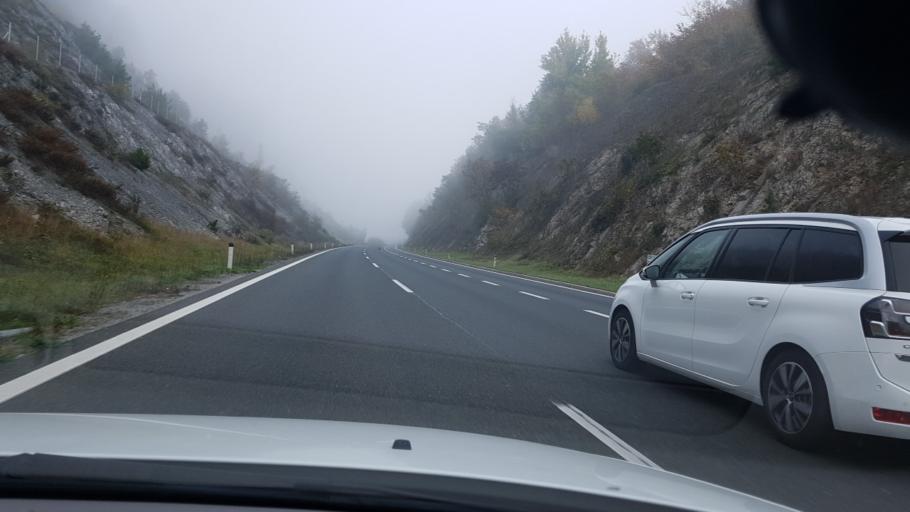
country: SI
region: Grosuplje
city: Grosuplje
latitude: 45.9664
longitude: 14.7265
